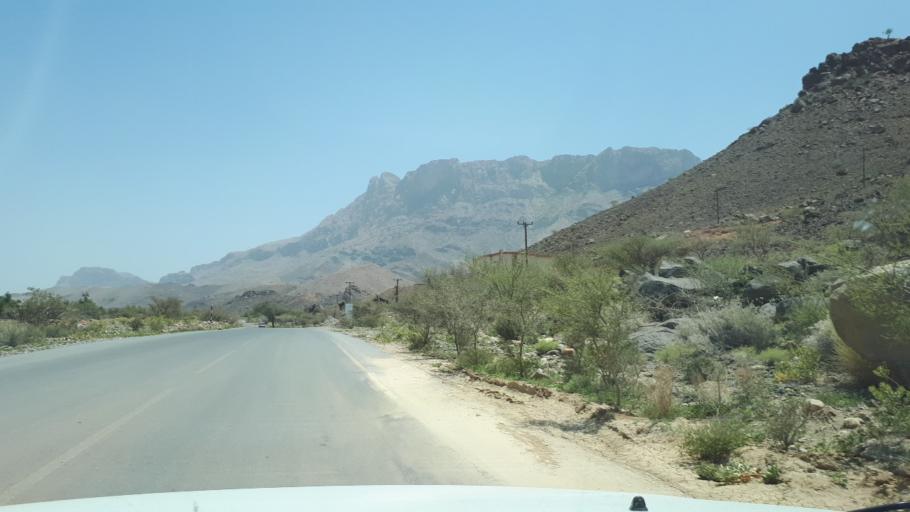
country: OM
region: Muhafazat ad Dakhiliyah
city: Bahla'
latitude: 23.1691
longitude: 57.1567
